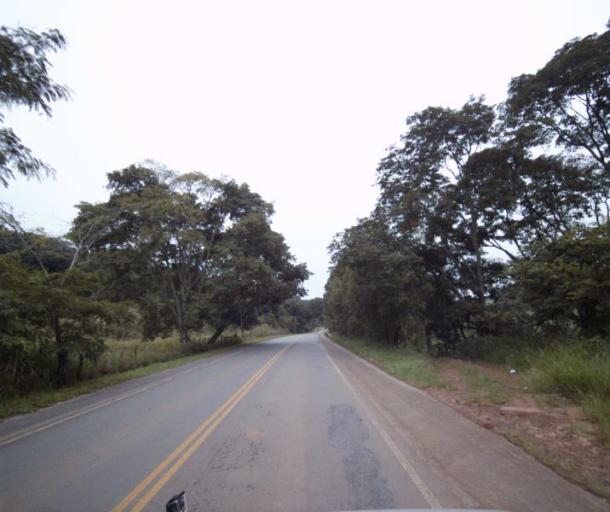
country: BR
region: Goias
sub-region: Pirenopolis
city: Pirenopolis
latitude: -15.9617
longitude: -48.8180
